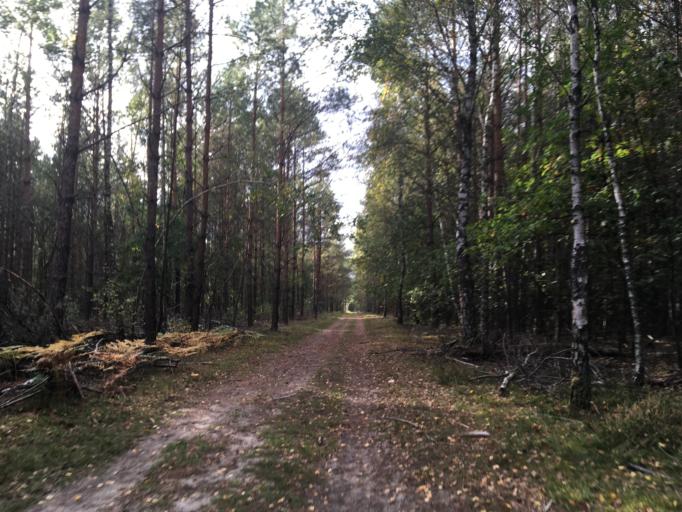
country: DE
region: Brandenburg
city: Glienicke
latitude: 52.6980
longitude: 13.3577
